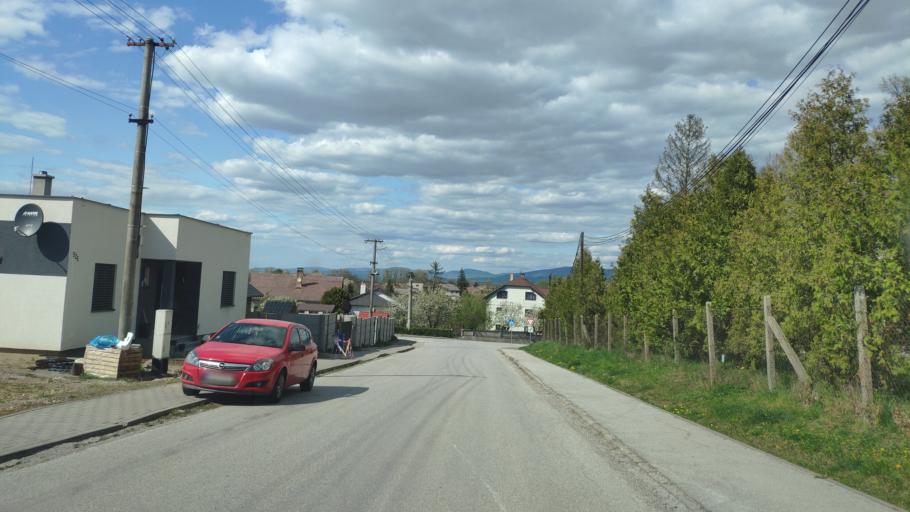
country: SK
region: Kosicky
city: Kosice
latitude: 48.6800
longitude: 21.4311
